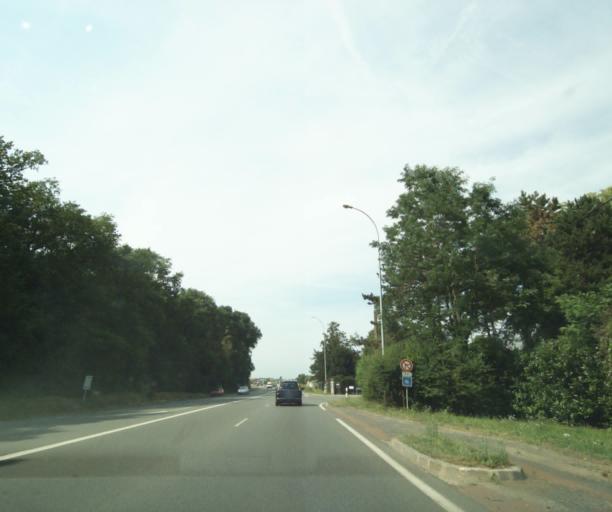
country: FR
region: Centre
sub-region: Departement d'Indre-et-Loire
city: Chambray-les-Tours
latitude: 47.3140
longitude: 0.7119
